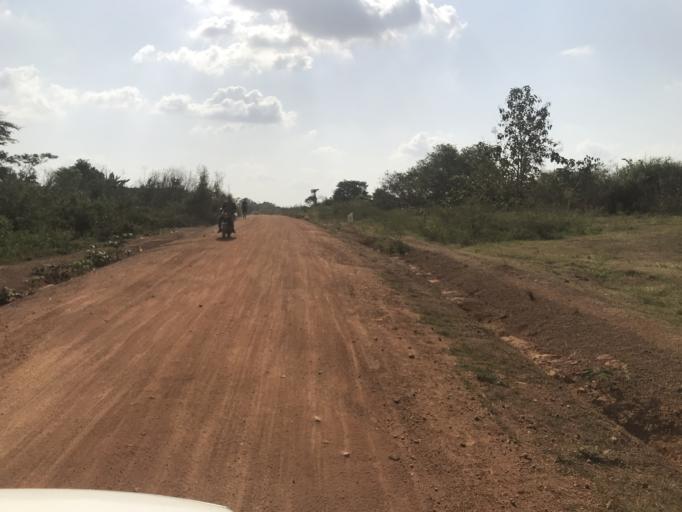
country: NG
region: Osun
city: Osogbo
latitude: 7.8267
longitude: 4.5703
